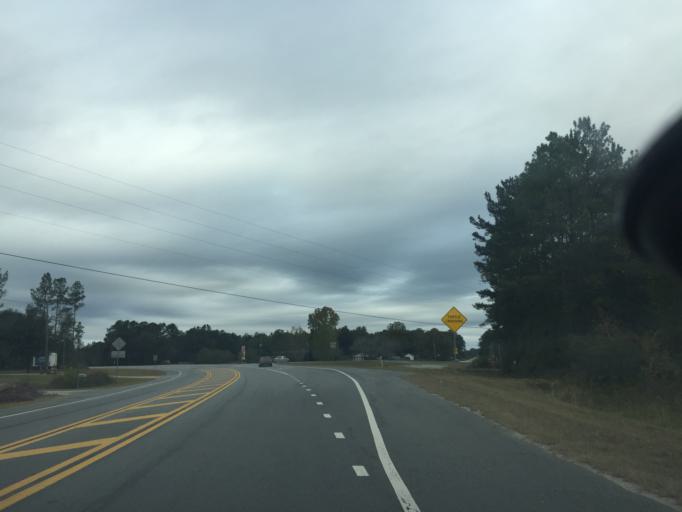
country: US
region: Georgia
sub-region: Chatham County
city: Bloomingdale
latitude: 32.0800
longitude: -81.3707
